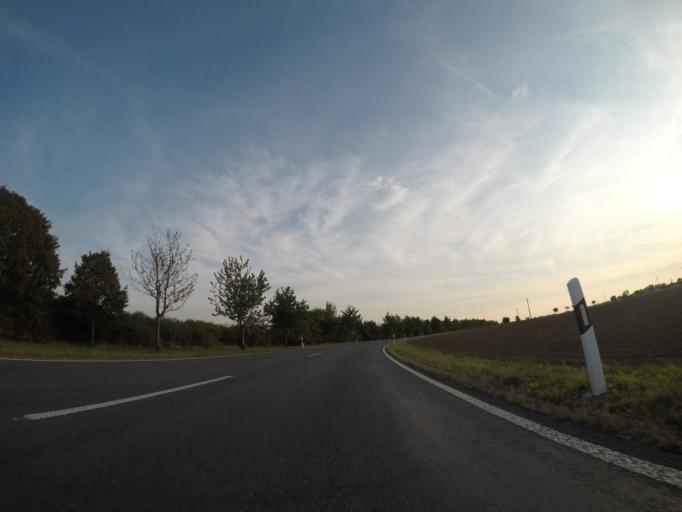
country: DE
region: Thuringia
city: Altkirchen
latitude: 50.9181
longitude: 12.3511
